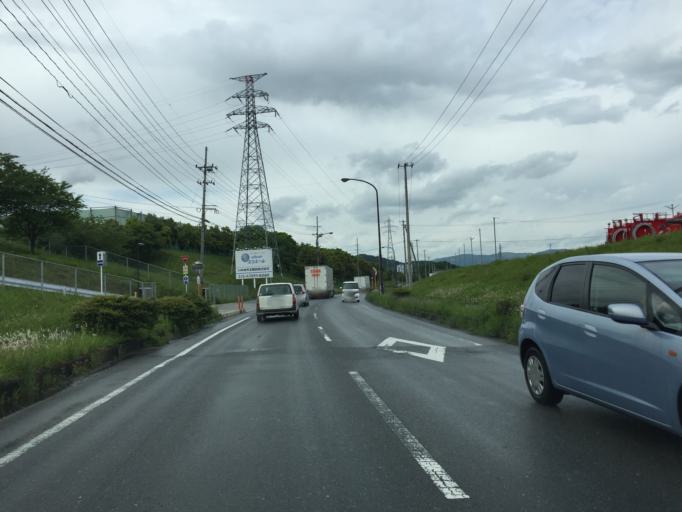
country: JP
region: Ibaraki
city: Kitaibaraki
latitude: 36.9346
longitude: 140.7471
